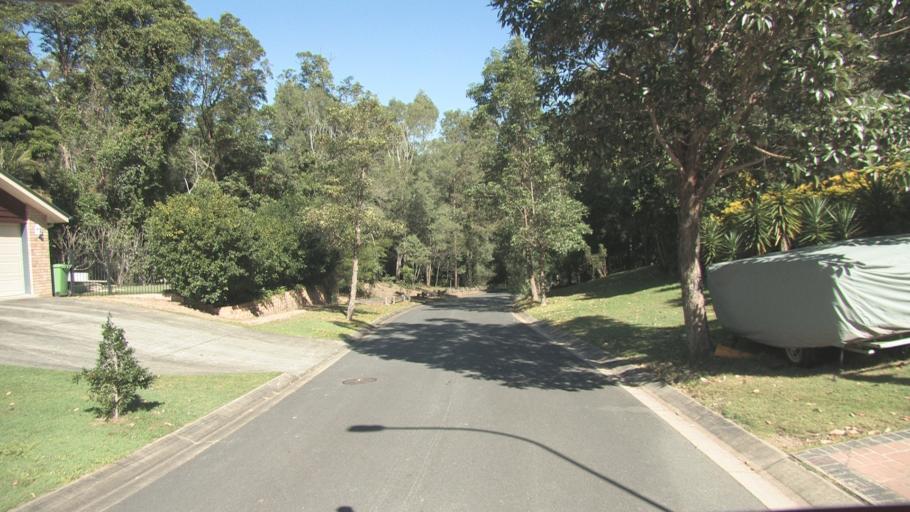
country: AU
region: Queensland
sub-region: Logan
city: Slacks Creek
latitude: -27.6375
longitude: 153.1774
